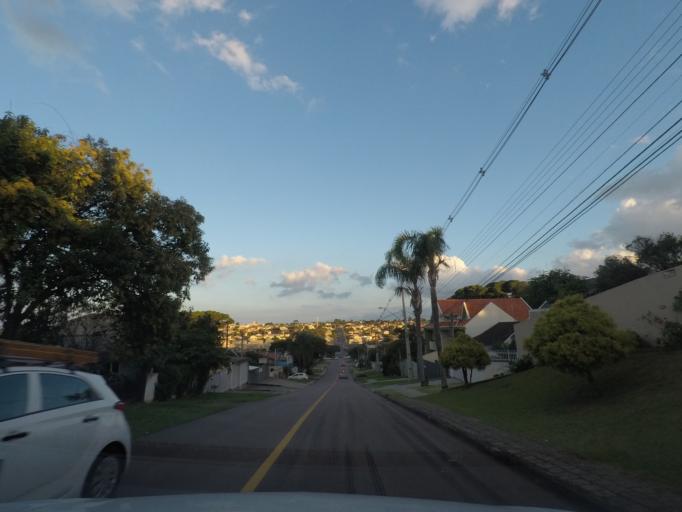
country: BR
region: Parana
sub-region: Sao Jose Dos Pinhais
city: Sao Jose dos Pinhais
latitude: -25.4941
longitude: -49.2578
